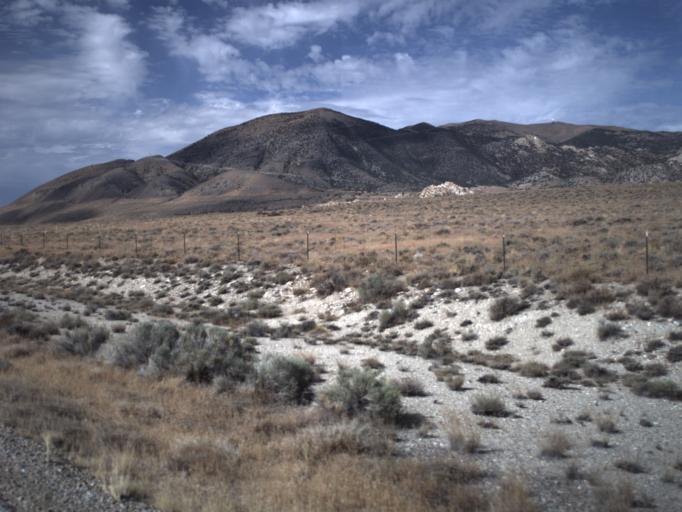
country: US
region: Utah
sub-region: Tooele County
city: Wendover
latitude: 41.4940
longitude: -113.6152
